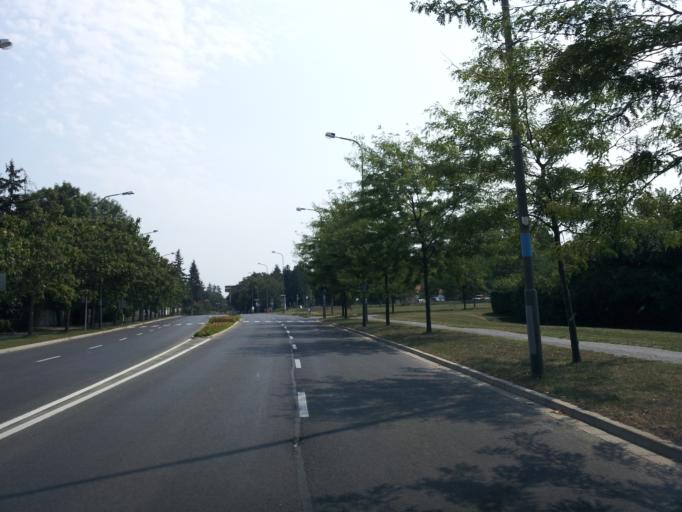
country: HU
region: Vas
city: Szombathely
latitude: 47.2317
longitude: 16.6031
